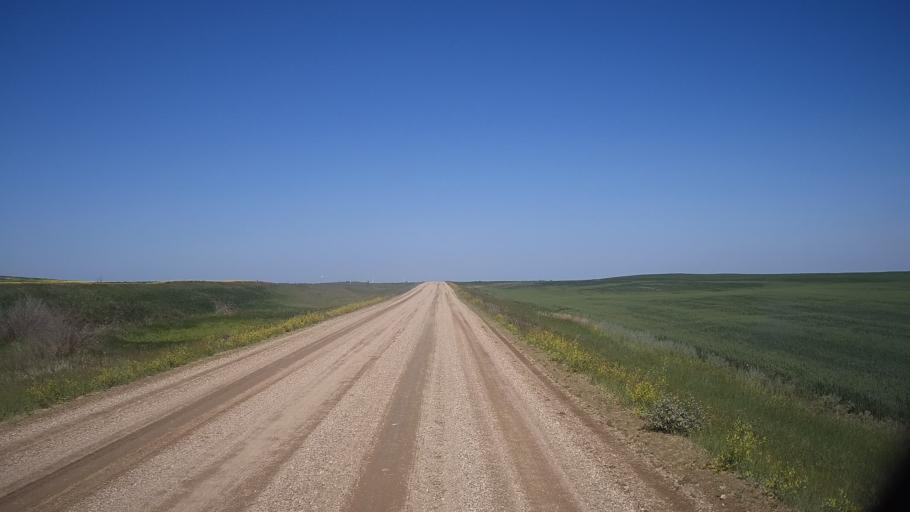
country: CA
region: Saskatchewan
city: Watrous
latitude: 51.8512
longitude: -105.9361
